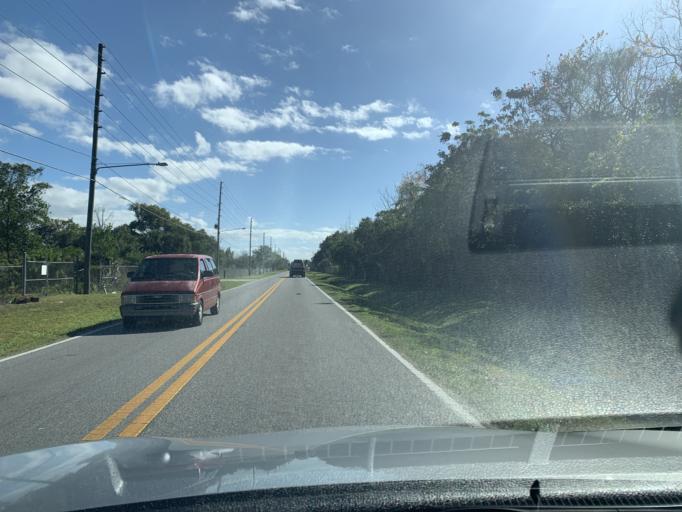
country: US
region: Florida
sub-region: Seminole County
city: Forest City
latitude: 28.6434
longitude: -81.4653
